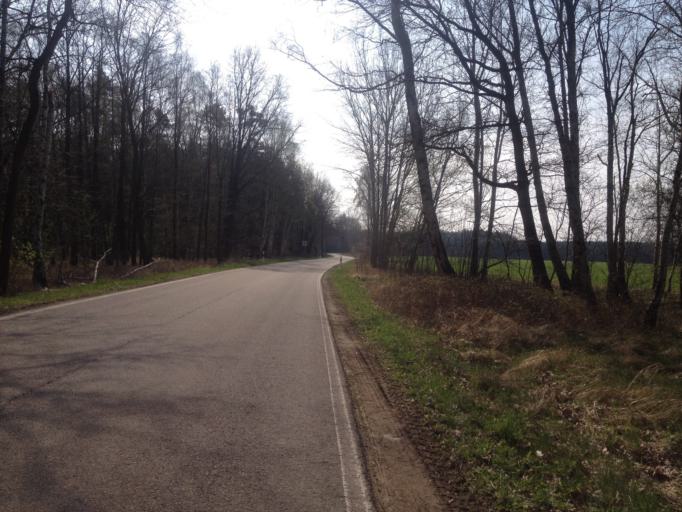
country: DE
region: Brandenburg
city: Drehnow
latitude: 51.8346
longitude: 14.3524
